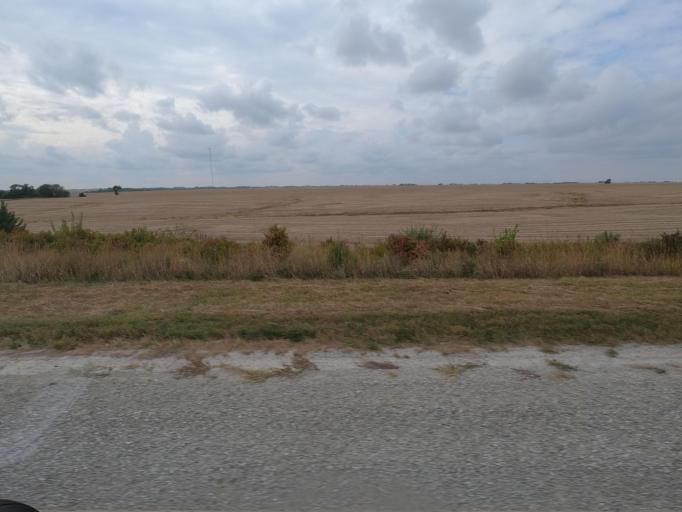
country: US
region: Iowa
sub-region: Jasper County
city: Monroe
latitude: 41.5322
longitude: -93.1304
